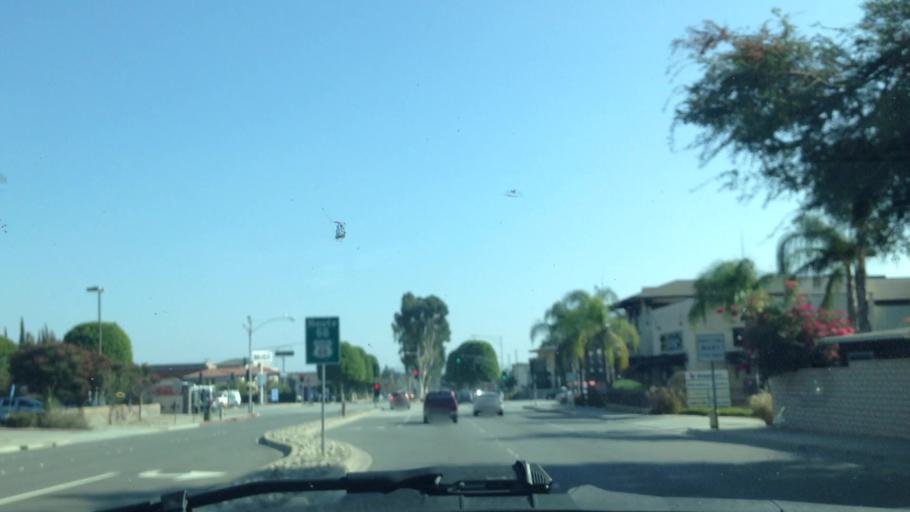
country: US
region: California
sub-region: Los Angeles County
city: Glendora
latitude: 34.1298
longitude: -117.8727
